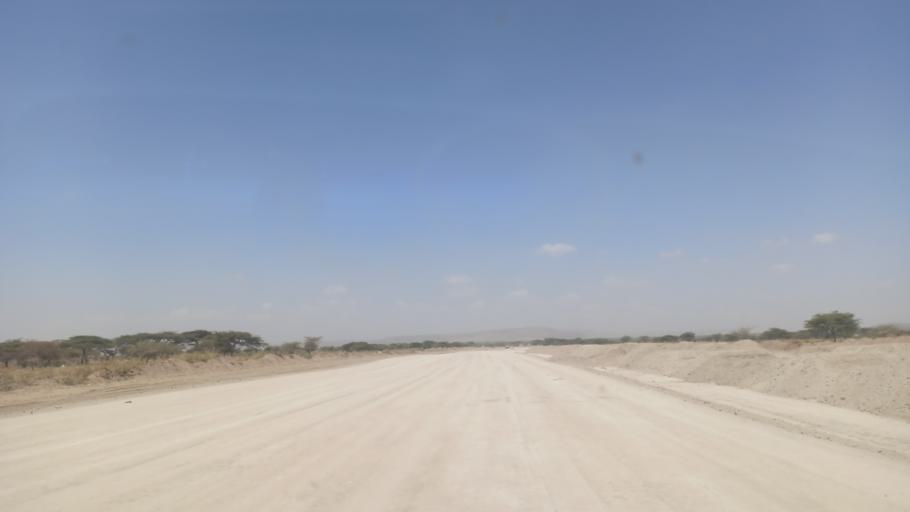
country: ET
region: Oromiya
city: Ziway
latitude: 7.7421
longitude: 38.6191
